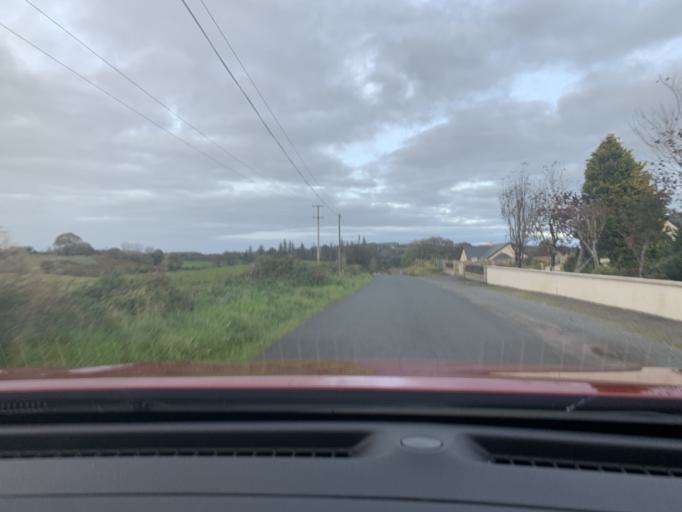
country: IE
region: Connaught
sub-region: Sligo
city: Tobercurry
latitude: 54.0321
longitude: -8.6976
